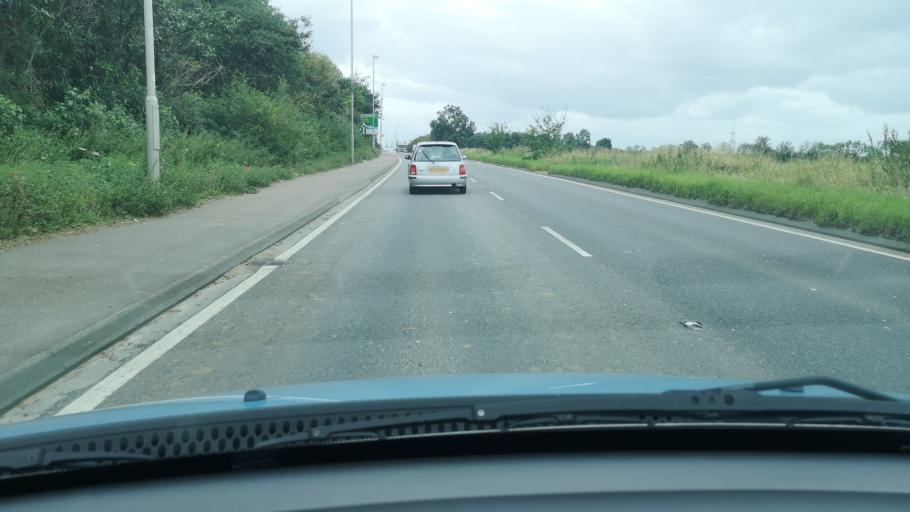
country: GB
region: England
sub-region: City and Borough of Wakefield
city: North Elmsall
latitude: 53.6056
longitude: -1.2724
